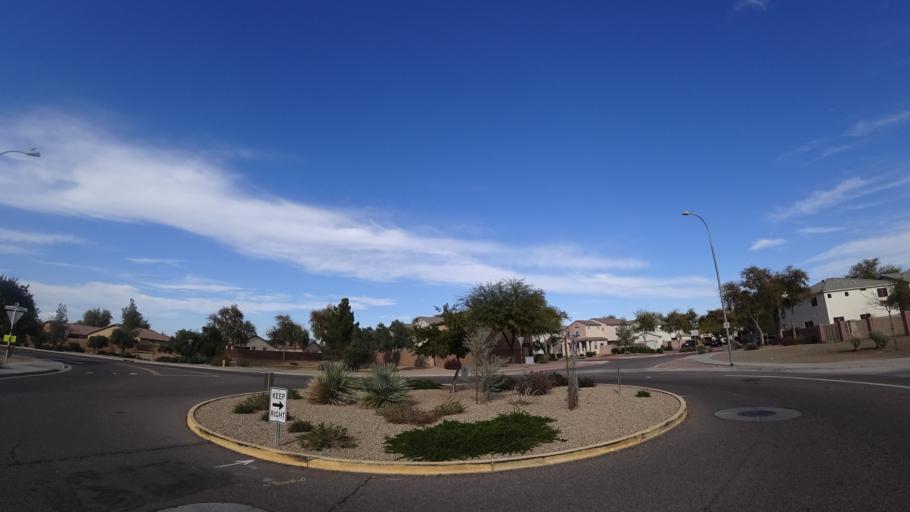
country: US
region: Arizona
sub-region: Maricopa County
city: Tolleson
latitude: 33.4183
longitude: -112.2786
